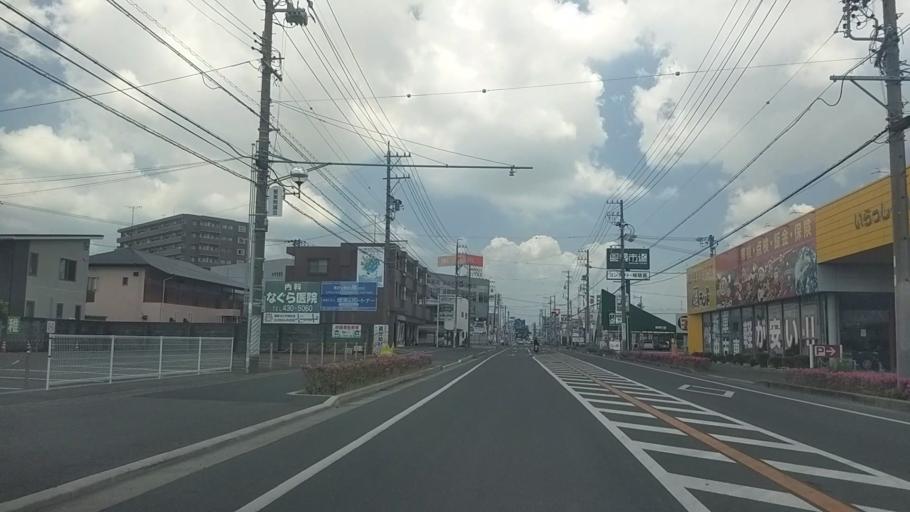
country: JP
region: Shizuoka
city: Hamamatsu
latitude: 34.7610
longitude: 137.7237
